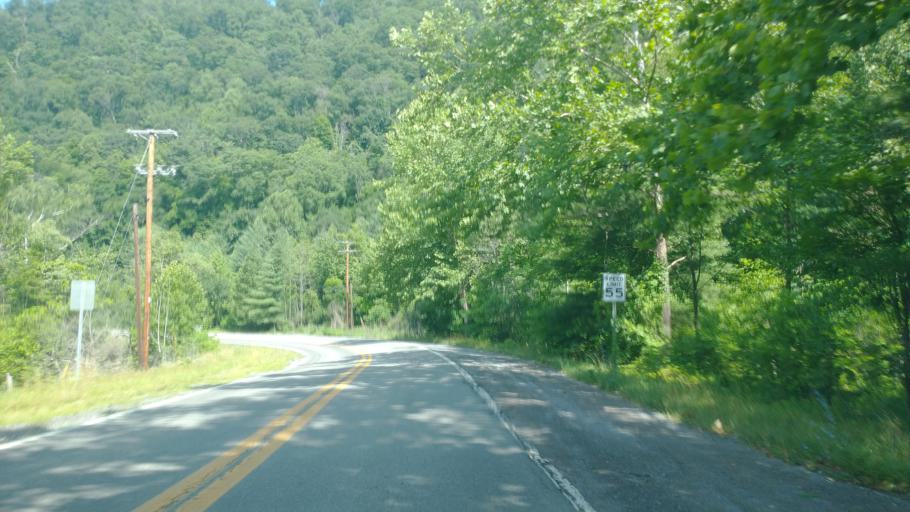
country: US
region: West Virginia
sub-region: McDowell County
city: Welch
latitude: 37.4145
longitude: -81.5244
